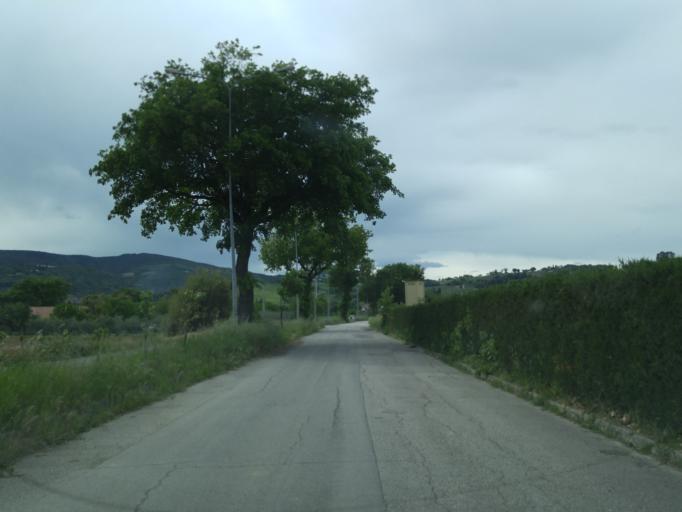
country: IT
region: The Marches
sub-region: Provincia di Pesaro e Urbino
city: Fossombrone
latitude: 43.6981
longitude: 12.8445
